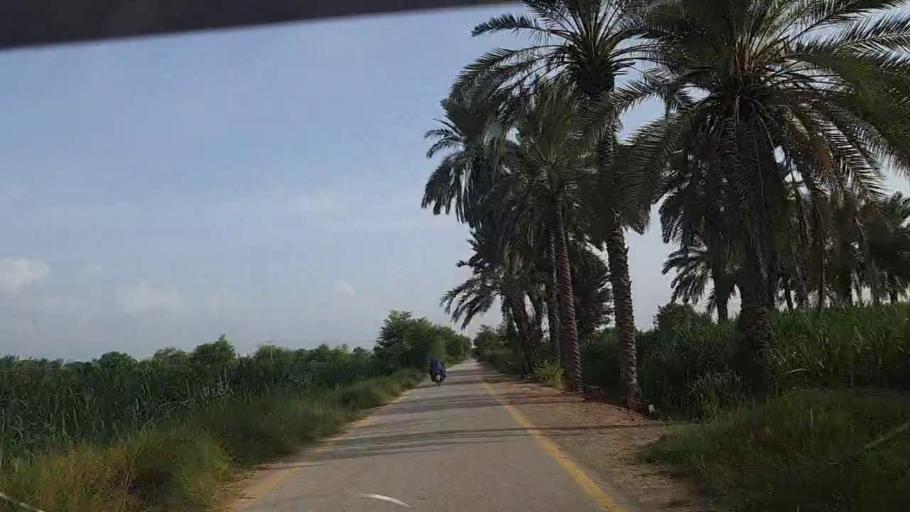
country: PK
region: Sindh
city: Ghotki
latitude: 27.9737
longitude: 69.2559
